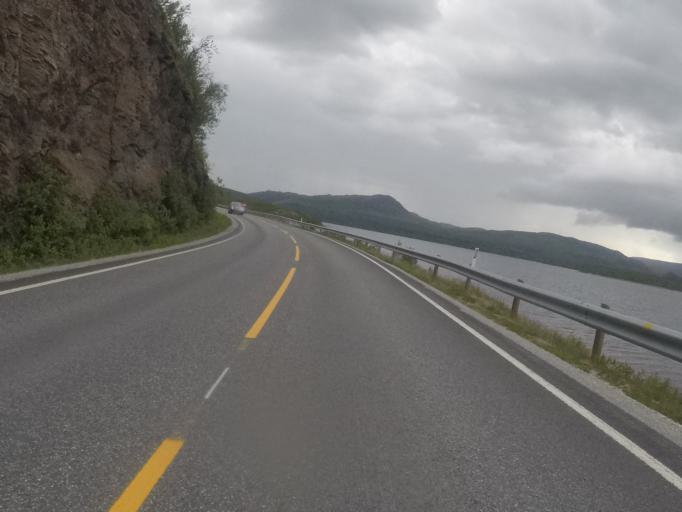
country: NO
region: Finnmark Fylke
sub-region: Porsanger
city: Lakselv
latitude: 69.9175
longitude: 24.9802
